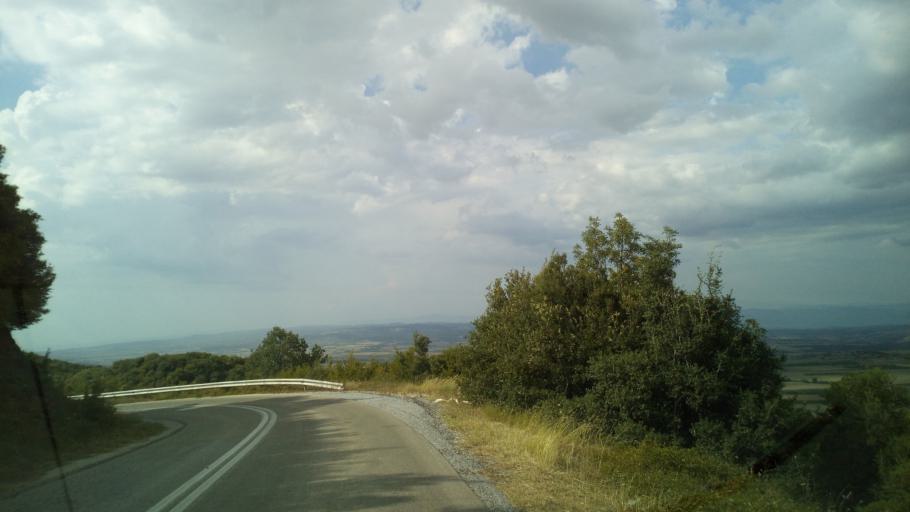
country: GR
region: Central Macedonia
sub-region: Nomos Chalkidikis
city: Galatista
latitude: 40.4909
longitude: 23.3933
